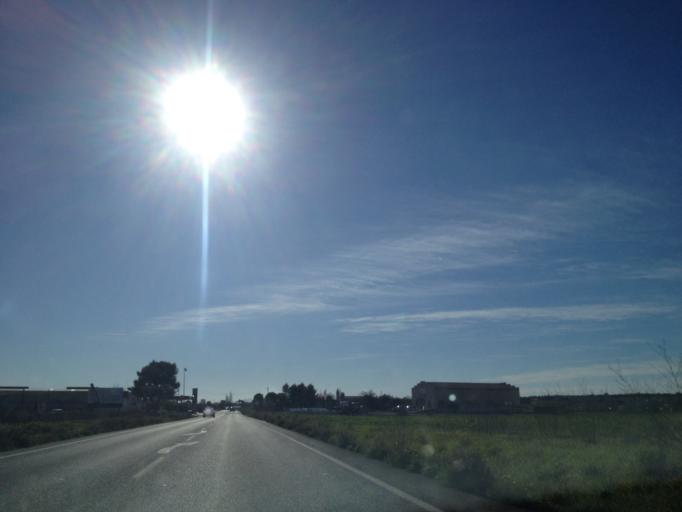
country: ES
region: Balearic Islands
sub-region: Illes Balears
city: Petra
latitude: 39.6282
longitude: 3.1076
